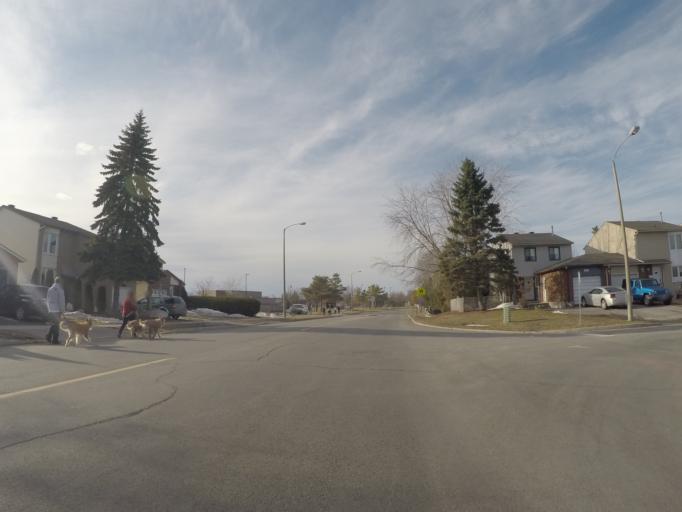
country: CA
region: Quebec
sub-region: Outaouais
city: Gatineau
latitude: 45.4661
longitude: -75.4971
